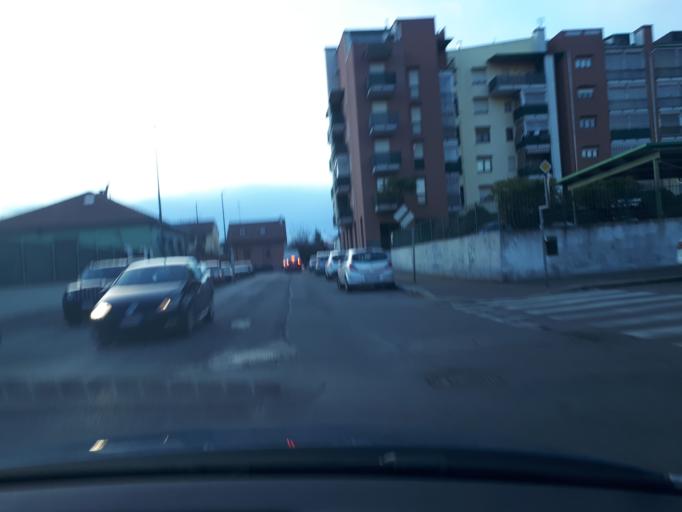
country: IT
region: Piedmont
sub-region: Provincia di Torino
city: Lesna
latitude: 45.0689
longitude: 7.6106
